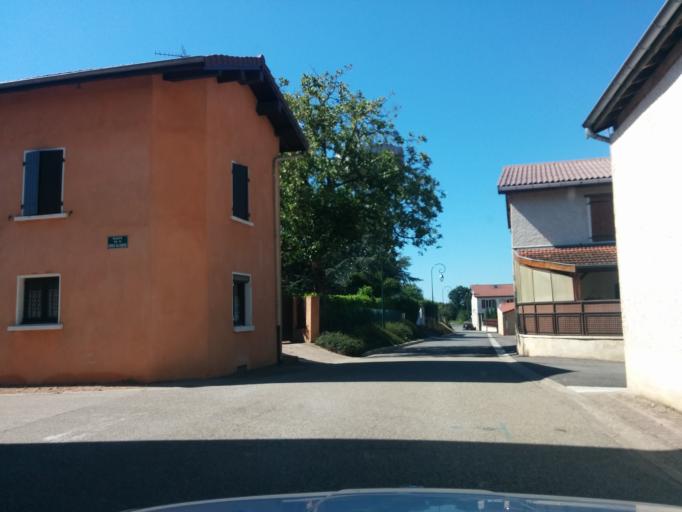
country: FR
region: Rhone-Alpes
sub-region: Departement de l'Ain
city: Perouges
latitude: 45.9334
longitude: 5.1523
